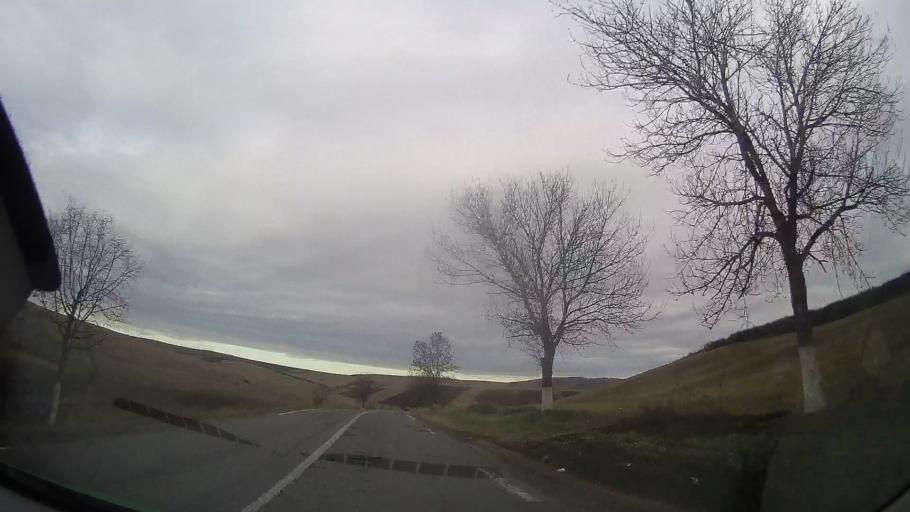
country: RO
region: Mures
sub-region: Comuna Faragau
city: Faragau
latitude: 46.7588
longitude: 24.5407
